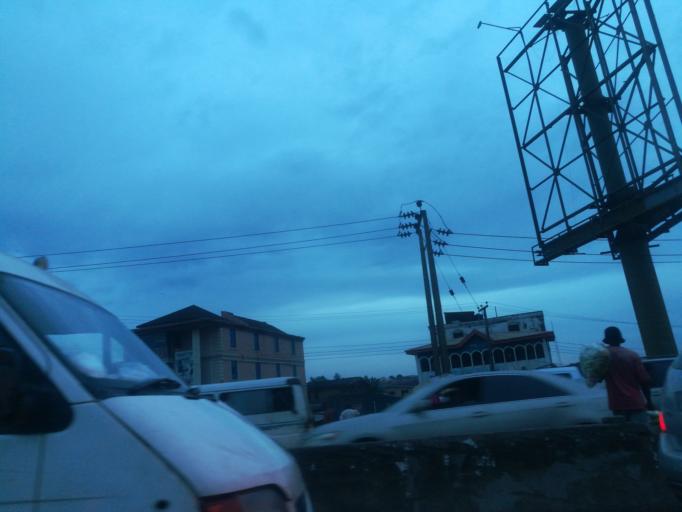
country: NG
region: Oyo
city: Ibadan
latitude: 7.4007
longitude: 3.9474
